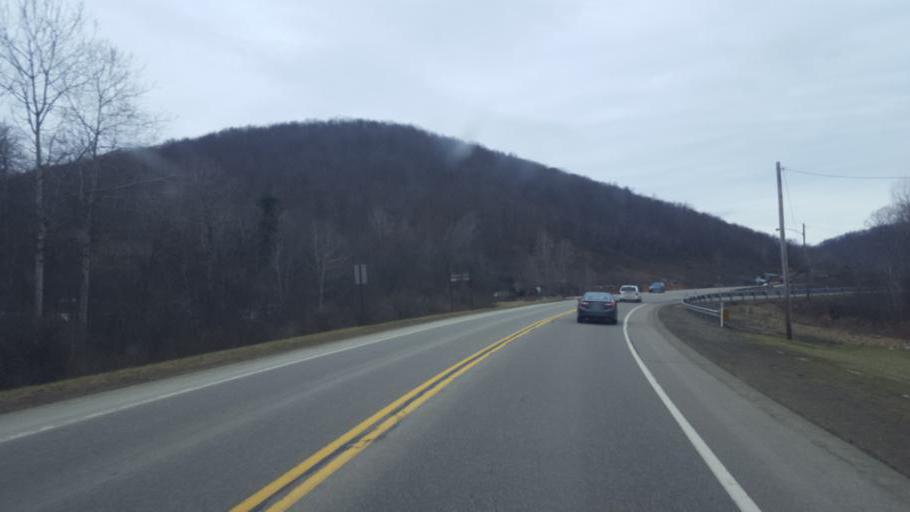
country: US
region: Pennsylvania
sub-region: Potter County
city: Coudersport
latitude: 41.7904
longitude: -78.0178
